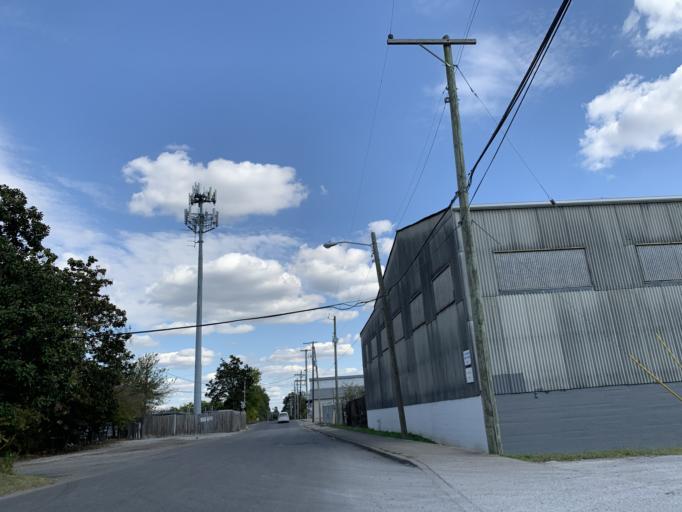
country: US
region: Kentucky
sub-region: Jefferson County
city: Louisville
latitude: 38.2453
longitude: -85.8037
